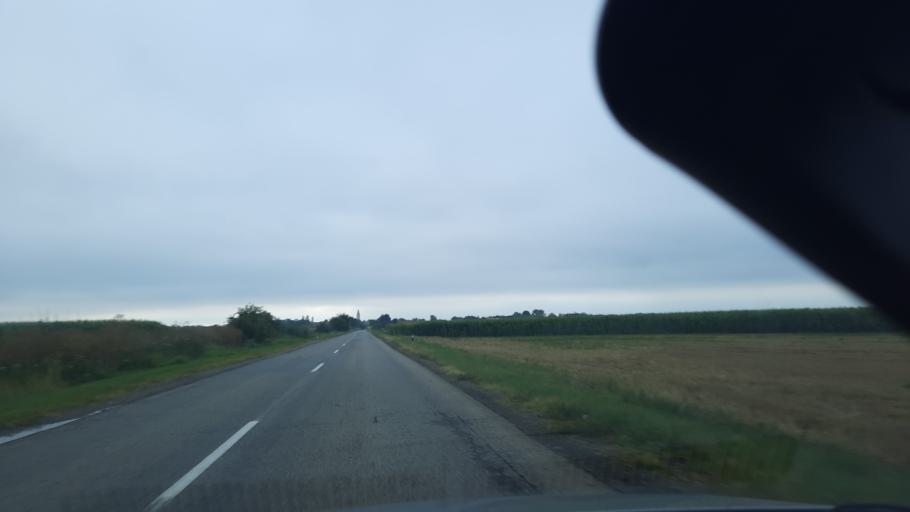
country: RS
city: Farkazdin
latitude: 45.1930
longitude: 20.4610
